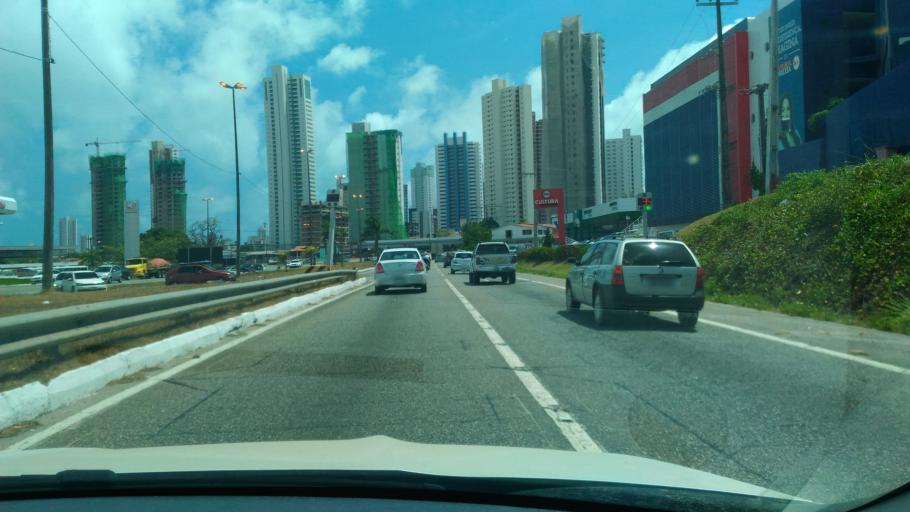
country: BR
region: Paraiba
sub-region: Joao Pessoa
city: Joao Pessoa
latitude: -7.1186
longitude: -34.8444
